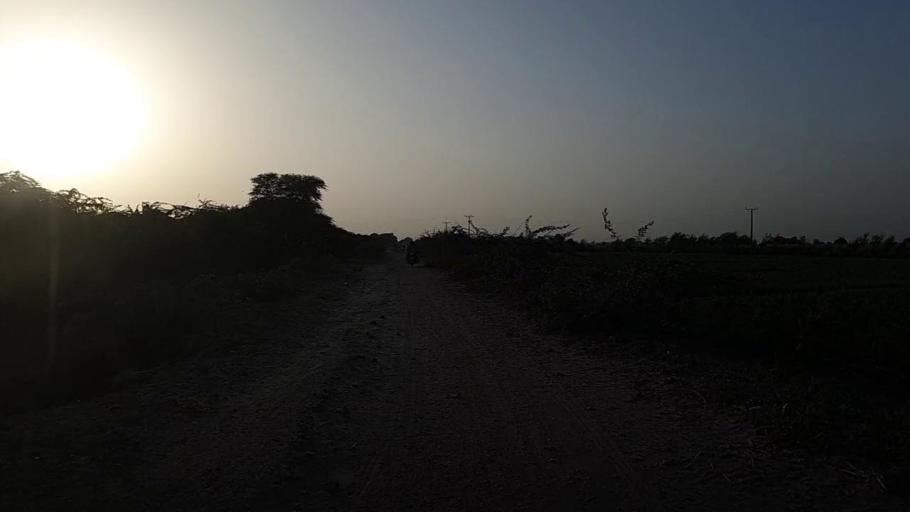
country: PK
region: Sindh
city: Kario
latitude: 24.7085
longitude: 68.4636
